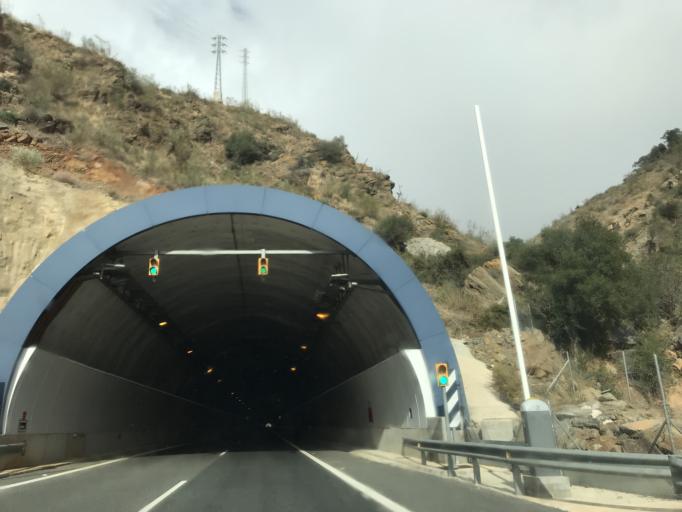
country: ES
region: Andalusia
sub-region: Provincia de Malaga
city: Almogia
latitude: 36.8577
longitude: -4.4847
